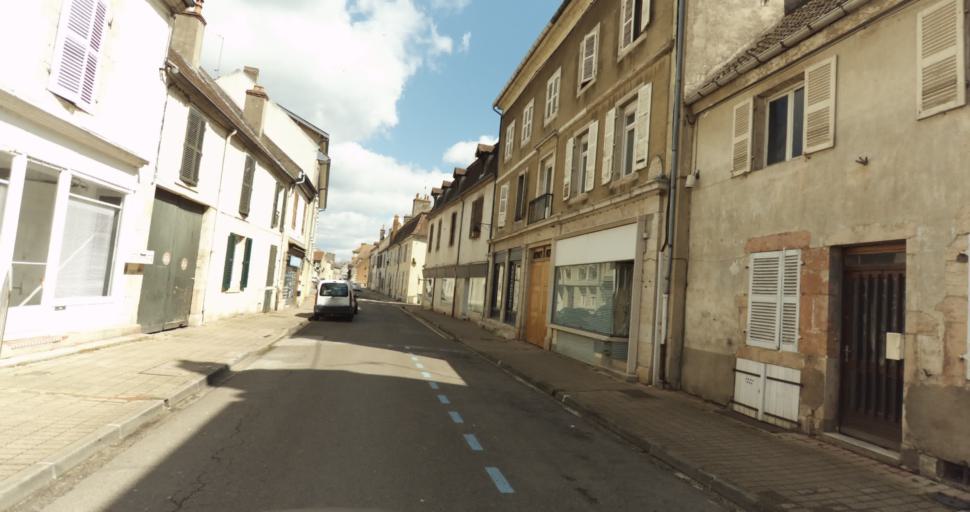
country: FR
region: Bourgogne
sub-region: Departement de la Cote-d'Or
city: Auxonne
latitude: 47.1939
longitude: 5.3862
